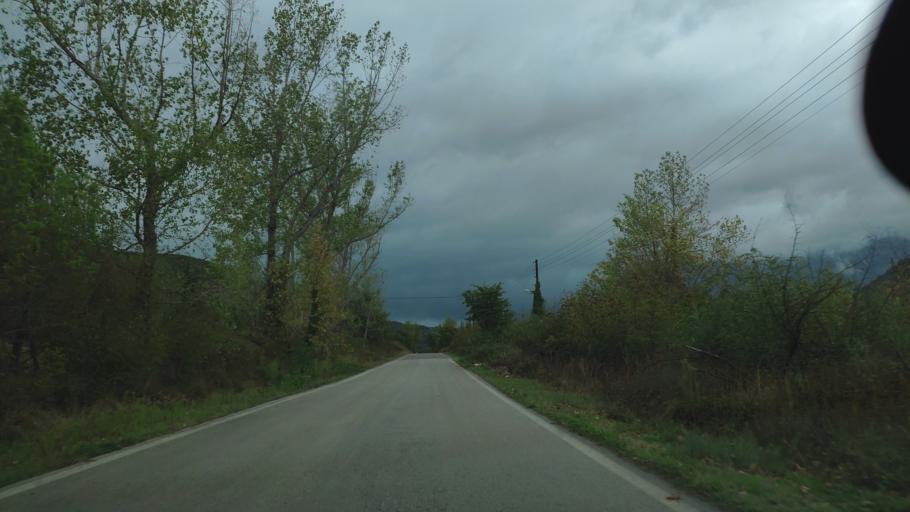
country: GR
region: West Greece
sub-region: Nomos Aitolias kai Akarnanias
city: Krikellos
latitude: 38.9897
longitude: 21.3159
